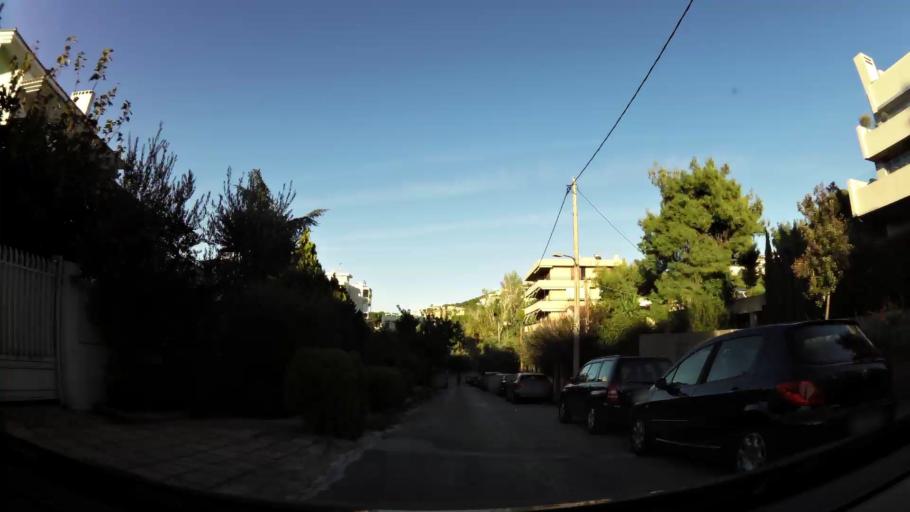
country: GR
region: Attica
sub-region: Nomarchia Athinas
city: Nea Erythraia
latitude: 38.0899
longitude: 23.8226
